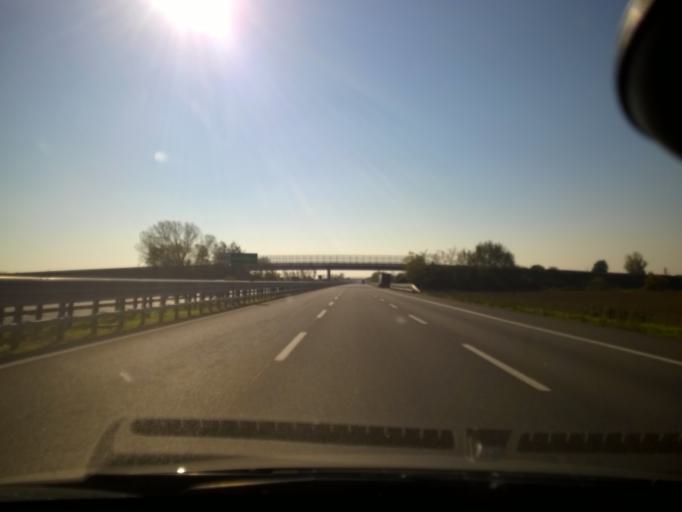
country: IT
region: Lombardy
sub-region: Provincia di Brescia
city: Bagnolo Mella
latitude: 45.4326
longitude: 10.2037
